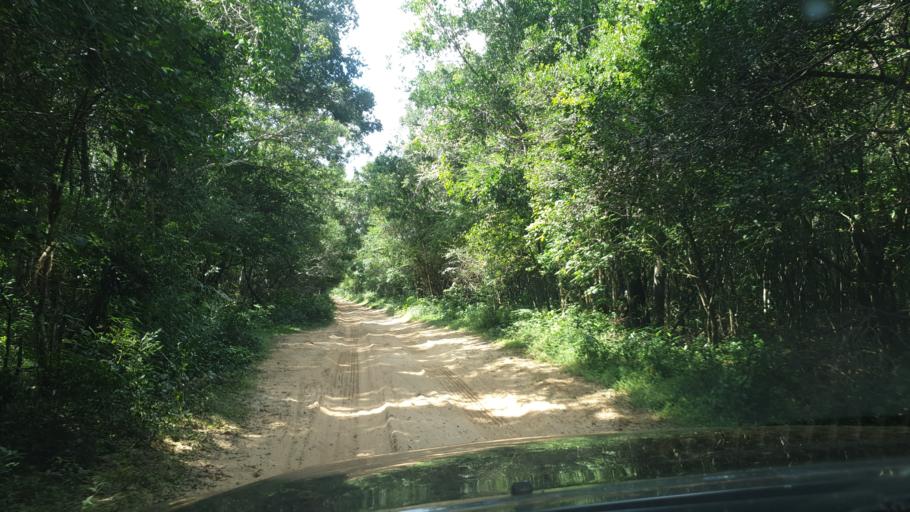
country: LK
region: North Central
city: Anuradhapura
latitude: 8.4178
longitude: 80.0217
